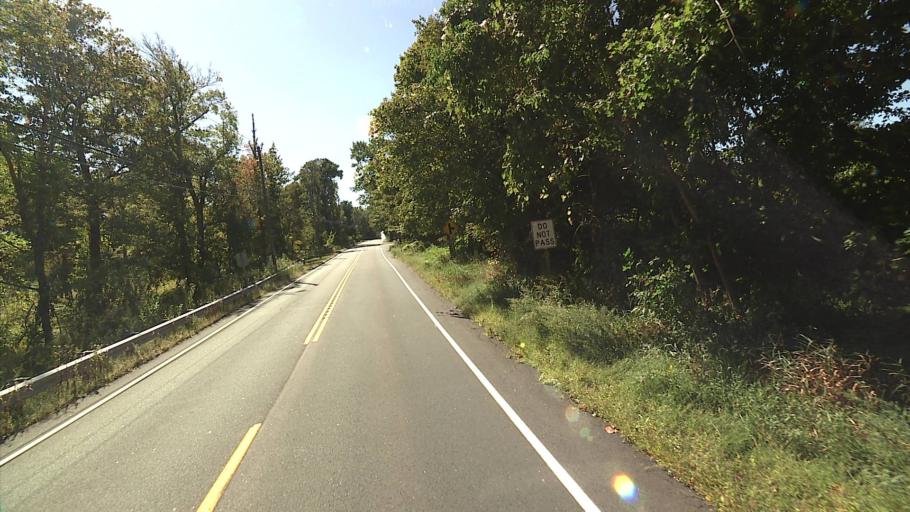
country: US
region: Connecticut
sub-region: New Haven County
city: Woodbridge
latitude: 41.4071
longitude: -72.9738
